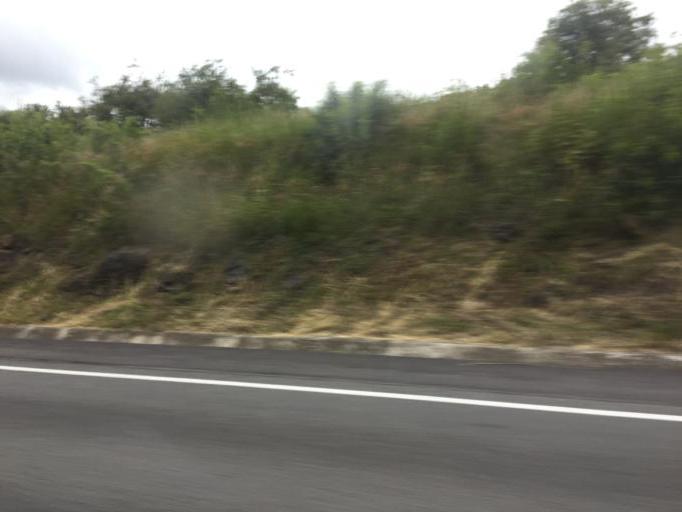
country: MX
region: Jalisco
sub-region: Zapotlan del Rey
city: Zapotlan del Rey
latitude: 20.5120
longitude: -102.9714
